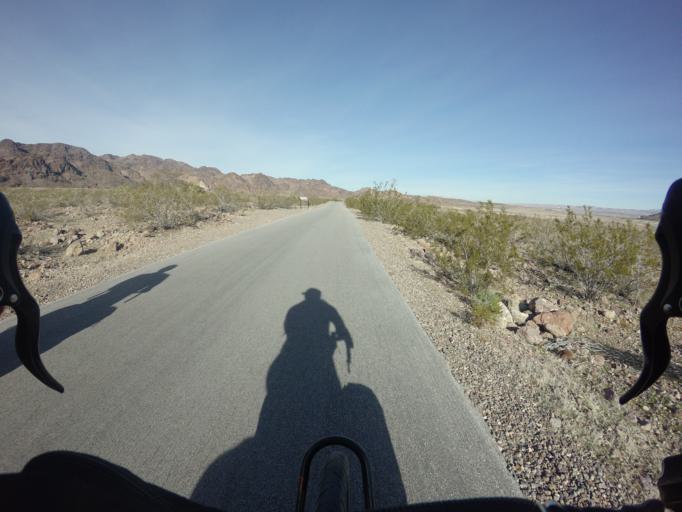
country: US
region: Nevada
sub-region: Clark County
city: Boulder City
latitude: 36.0437
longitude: -114.8087
